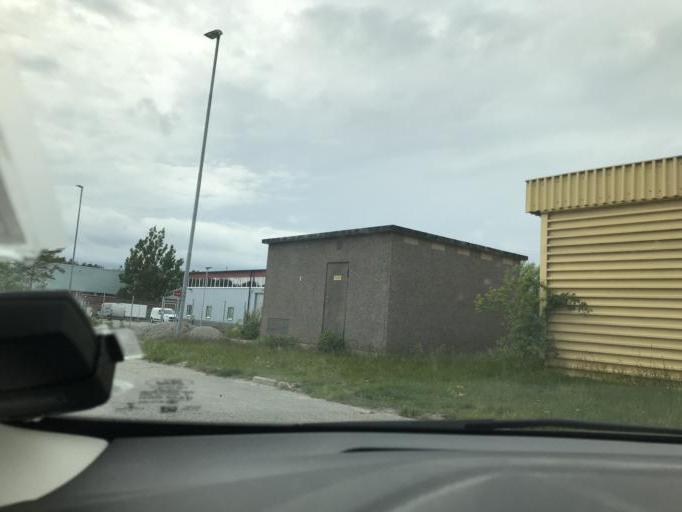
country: SE
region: Stockholm
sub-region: Botkyrka Kommun
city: Alby
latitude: 59.2331
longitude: 17.8366
